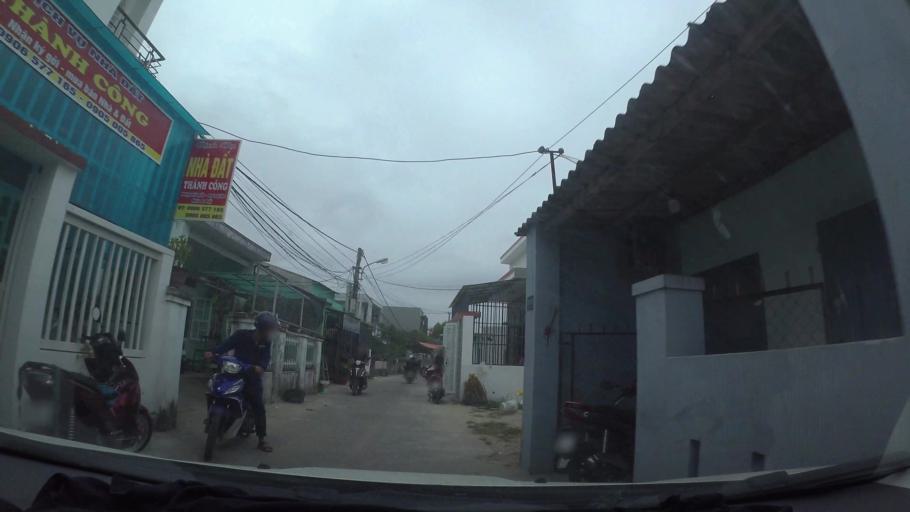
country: VN
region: Da Nang
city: Lien Chieu
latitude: 16.0840
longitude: 108.1552
